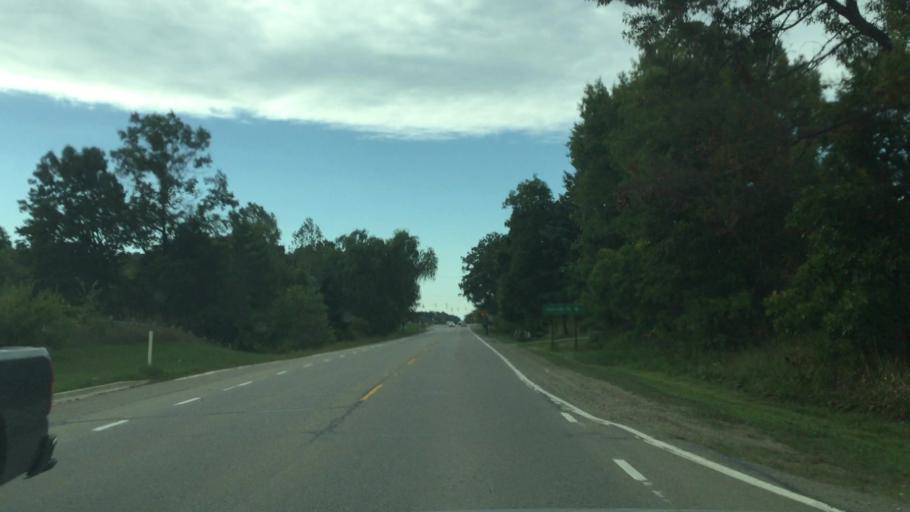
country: US
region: Michigan
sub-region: Livingston County
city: Howell
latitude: 42.6322
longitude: -83.8756
